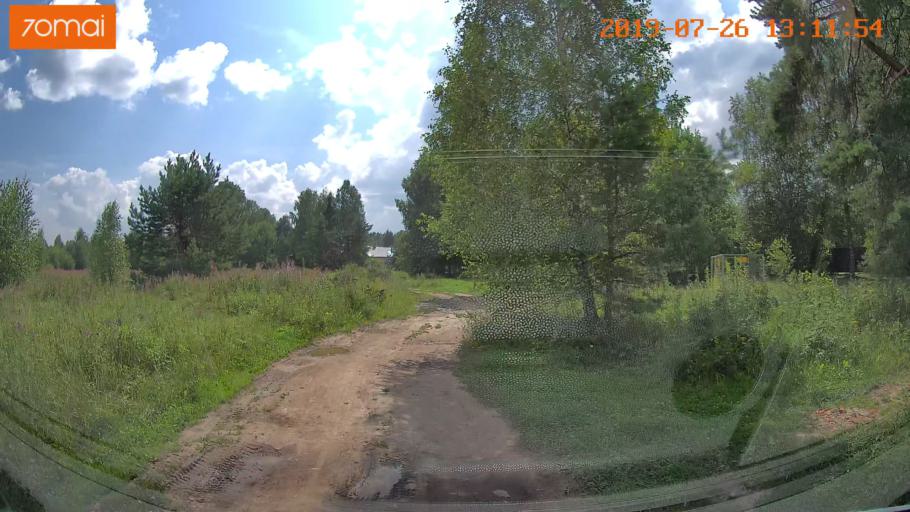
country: RU
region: Ivanovo
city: Bogorodskoye
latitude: 57.0598
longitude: 41.0559
